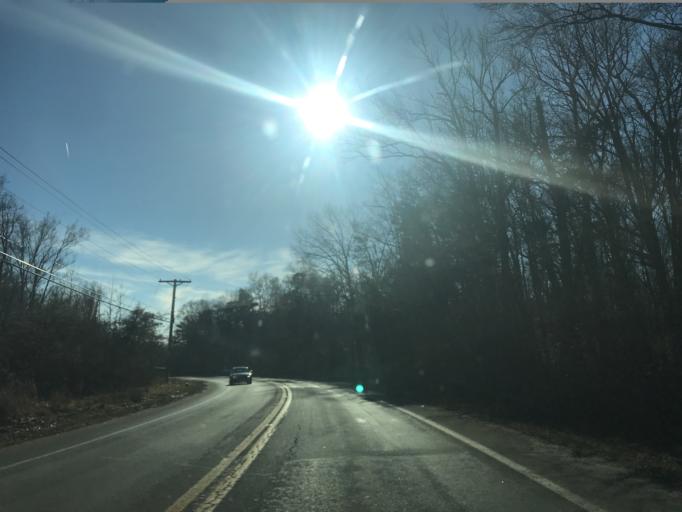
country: US
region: Maryland
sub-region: Prince George's County
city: Brandywine
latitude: 38.6958
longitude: -76.8860
